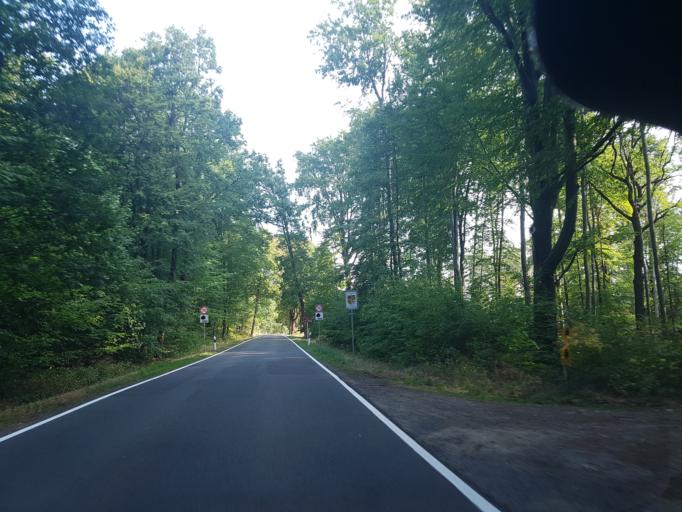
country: DE
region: Brandenburg
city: Wiesenburg
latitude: 52.0447
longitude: 12.3777
